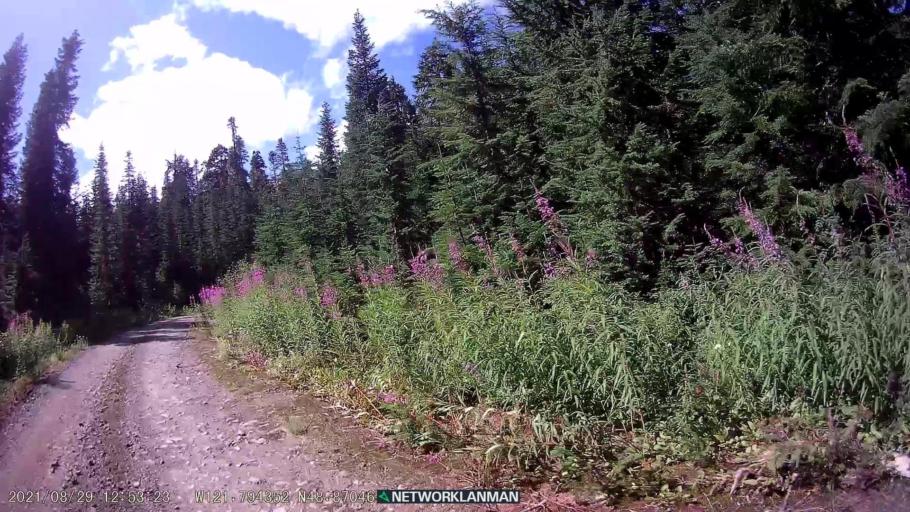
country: CA
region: British Columbia
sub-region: Fraser Valley Regional District
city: Chilliwack
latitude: 48.8704
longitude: -121.7946
